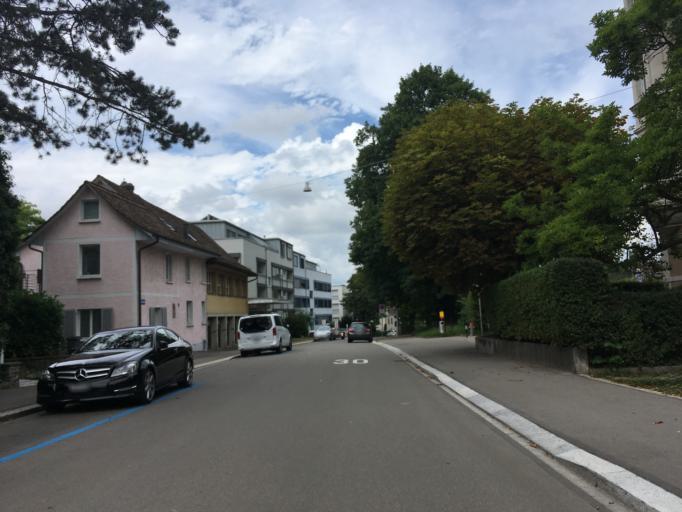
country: CH
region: Zurich
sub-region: Bezirk Zuerich
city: Zuerich (Kreis 7) / Fluntern
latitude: 47.3800
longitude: 8.5528
